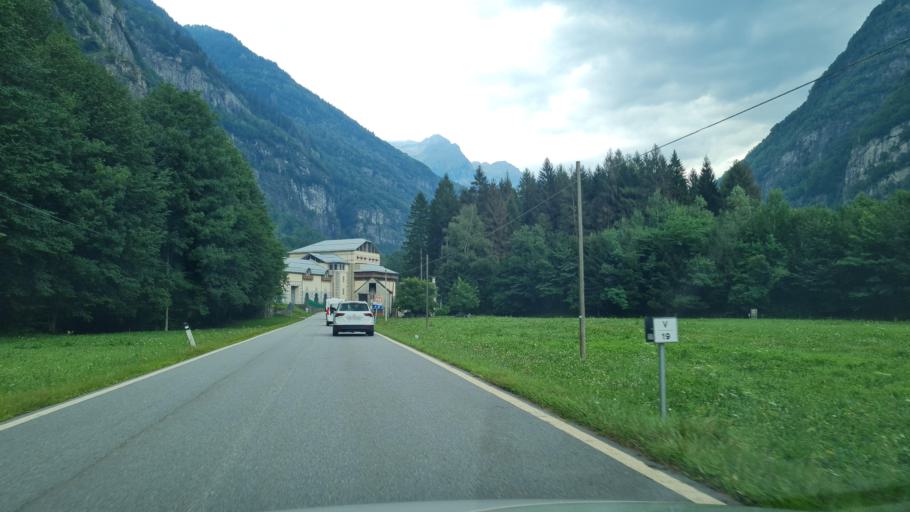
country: IT
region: Piedmont
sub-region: Provincia Verbano-Cusio-Ossola
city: Premia
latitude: 46.2873
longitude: 8.3549
